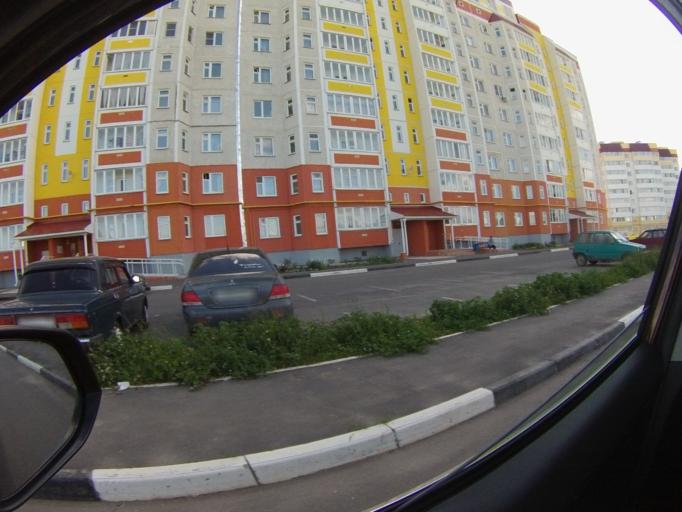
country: RU
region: Orjol
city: Mtsensk
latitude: 53.2933
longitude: 36.6082
